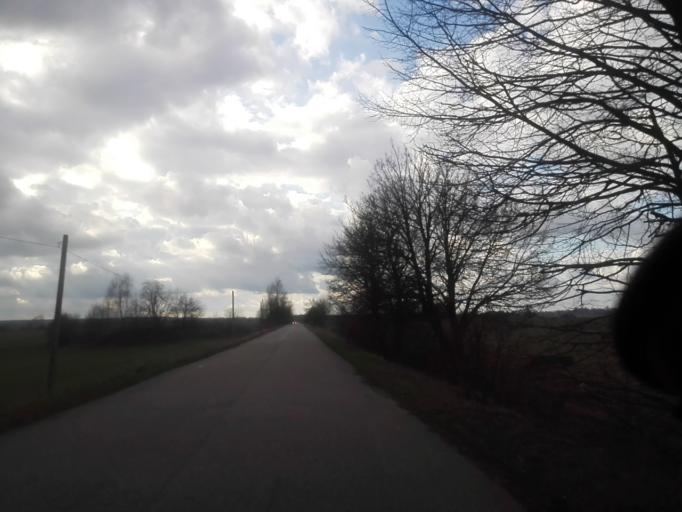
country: PL
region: Podlasie
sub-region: Suwalki
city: Suwalki
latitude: 54.2190
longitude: 22.8482
